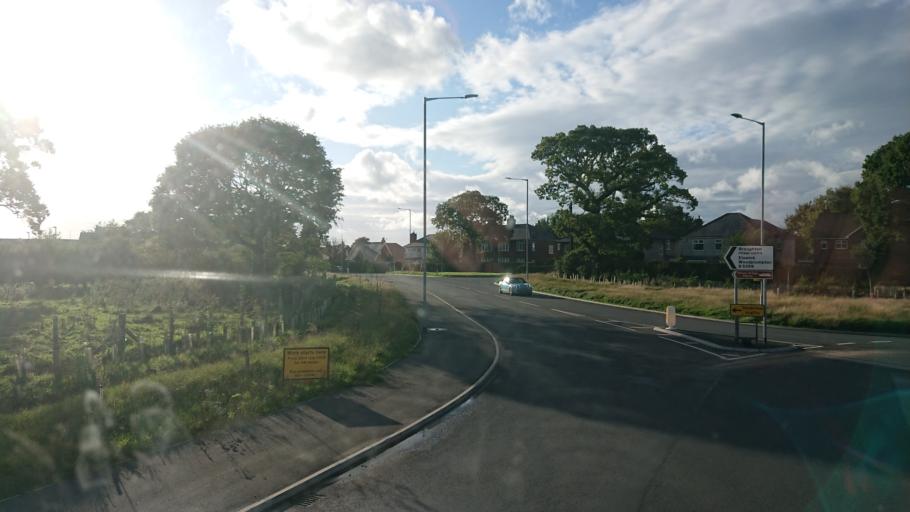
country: GB
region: England
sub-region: Lancashire
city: Preston
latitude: 53.8110
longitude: -2.7183
